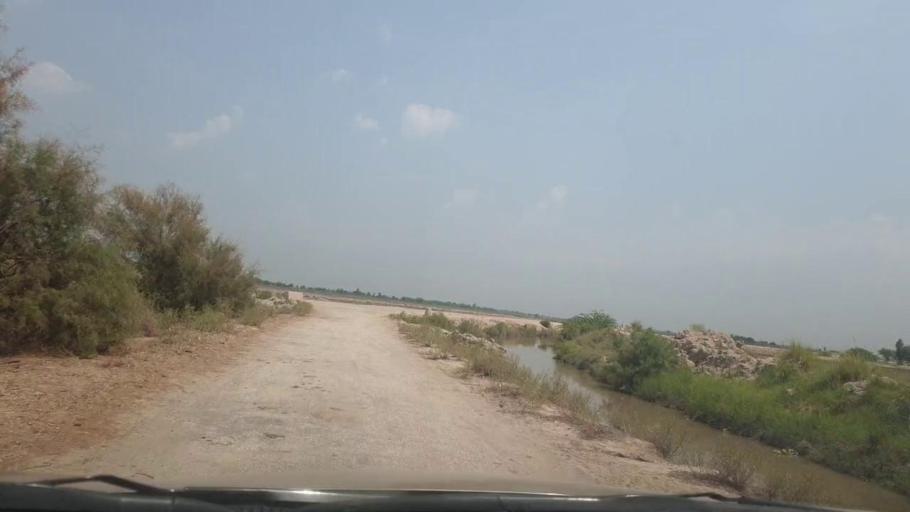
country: PK
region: Sindh
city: Ratodero
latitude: 27.6986
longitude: 68.2331
